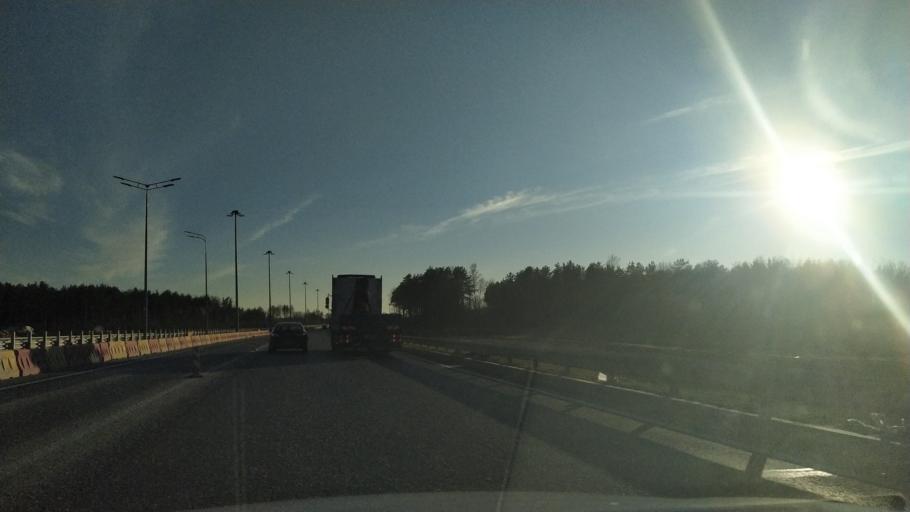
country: RU
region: St.-Petersburg
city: Levashovo
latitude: 60.0861
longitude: 30.2275
